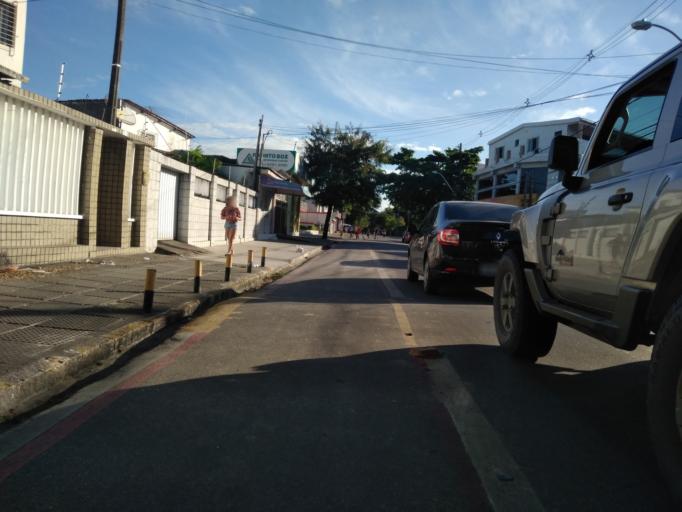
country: BR
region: Pernambuco
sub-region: Recife
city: Recife
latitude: -8.0801
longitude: -34.9354
